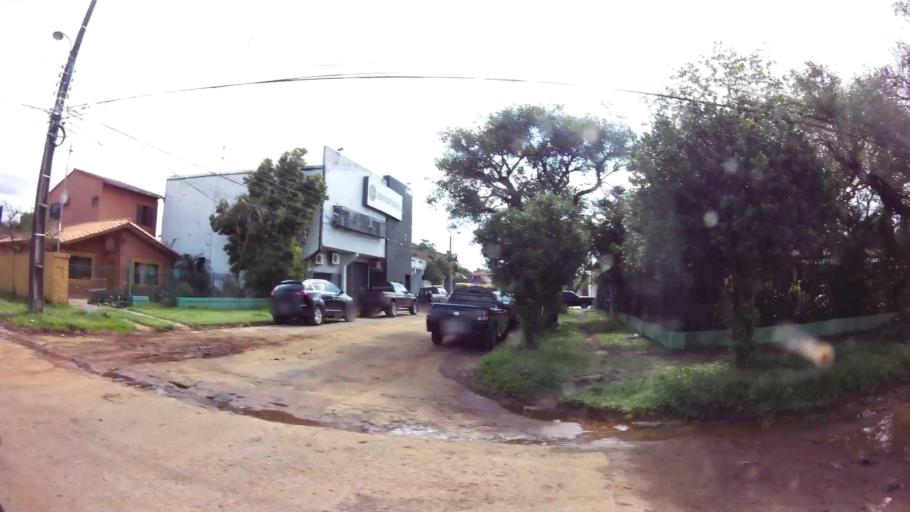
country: PY
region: Central
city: San Lorenzo
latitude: -25.2661
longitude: -57.5030
